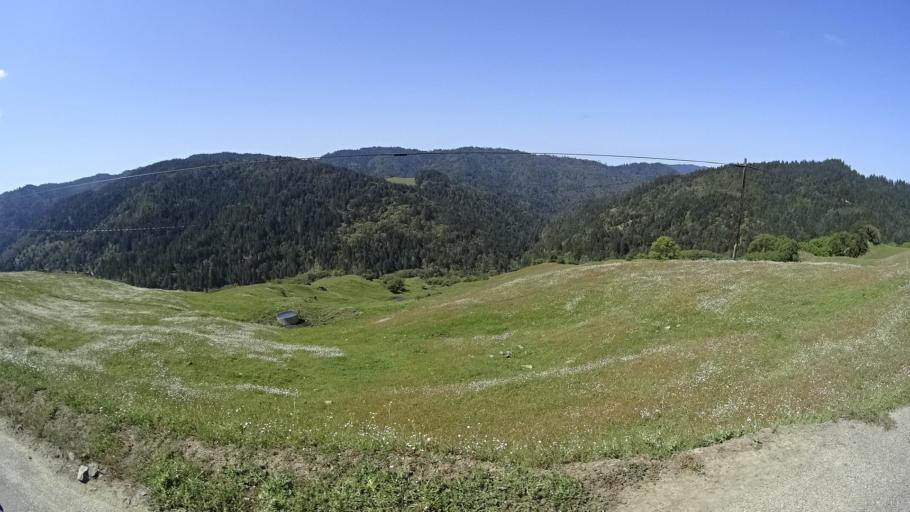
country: US
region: California
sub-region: Humboldt County
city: Redway
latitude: 40.0244
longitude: -123.6304
